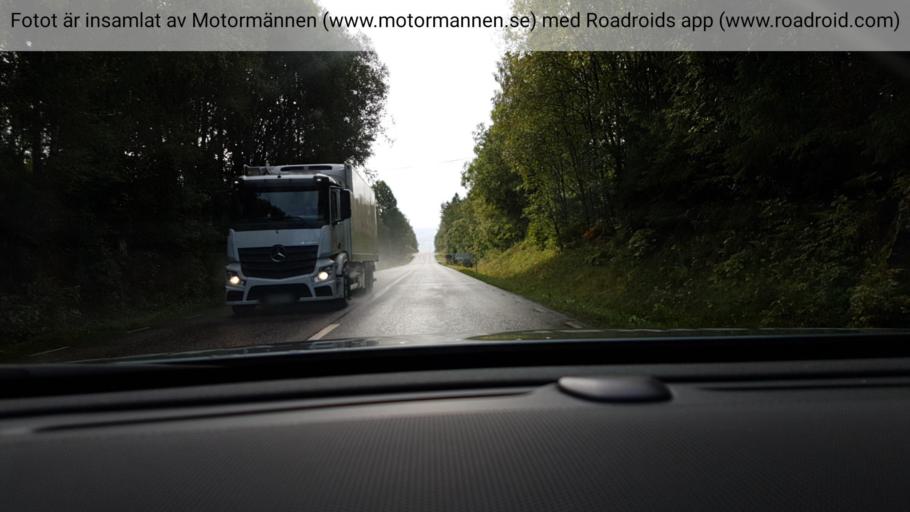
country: SE
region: Vaestra Goetaland
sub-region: Harryda Kommun
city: Ravlanda
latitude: 57.5680
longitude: 12.5103
